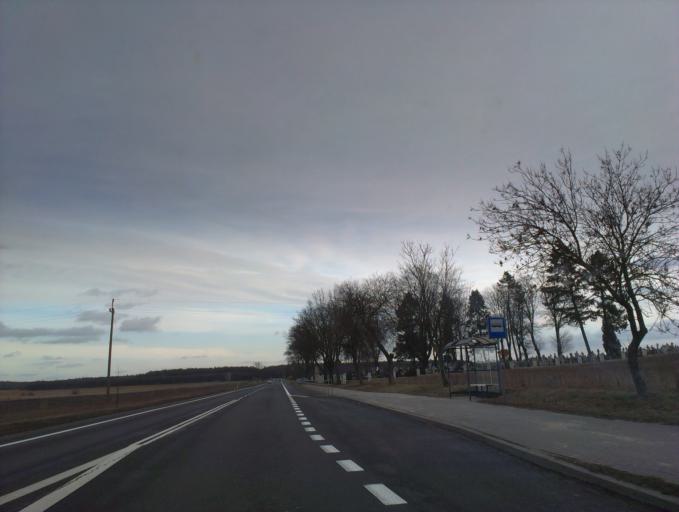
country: PL
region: Masovian Voivodeship
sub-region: Powiat sierpecki
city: Szczutowo
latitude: 52.8990
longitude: 19.5354
